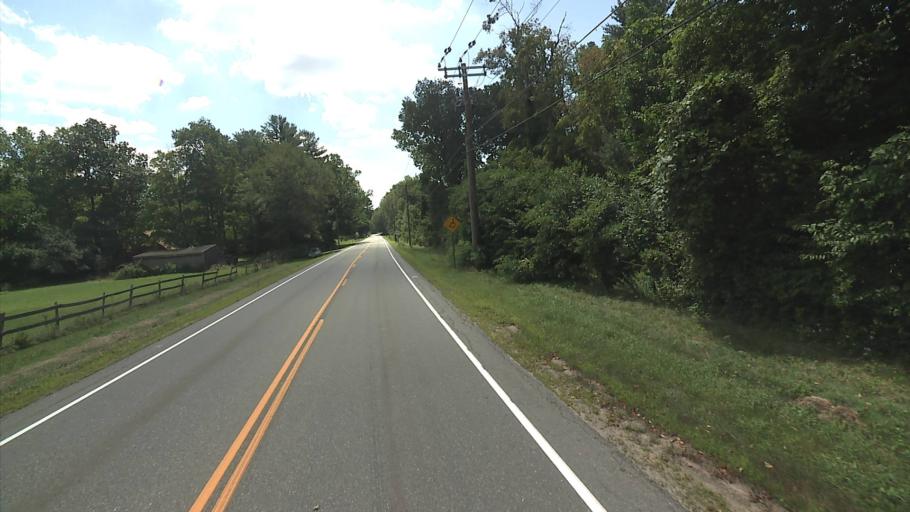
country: US
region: Massachusetts
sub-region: Worcester County
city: Southbridge
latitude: 41.9681
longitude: -72.0812
